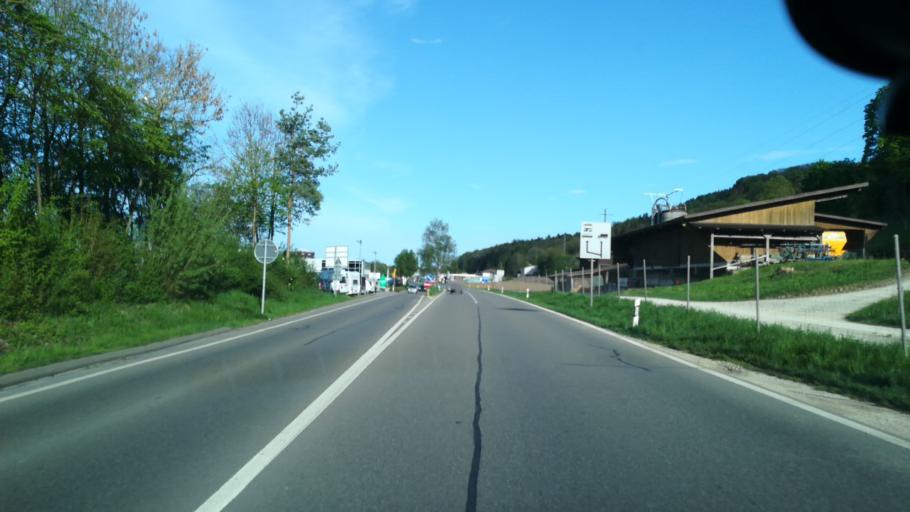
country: CH
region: Schaffhausen
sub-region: Bezirk Reiat
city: Thayngen
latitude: 47.7414
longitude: 8.7088
